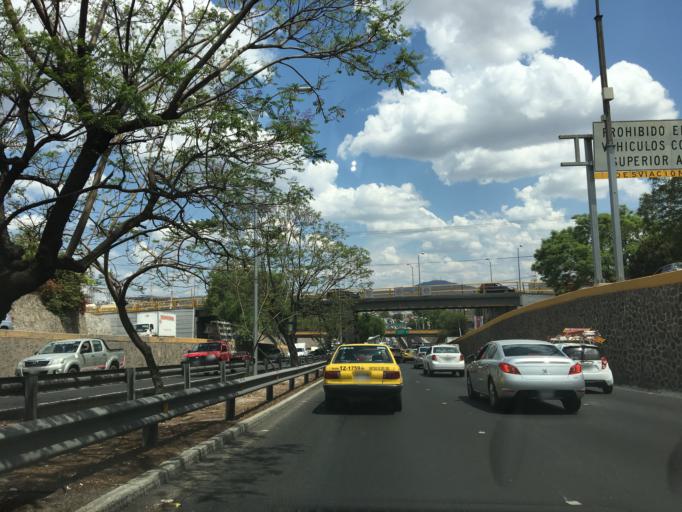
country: MX
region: Queretaro
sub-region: Queretaro
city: Santiago de Queretaro
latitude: 20.6052
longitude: -100.3775
